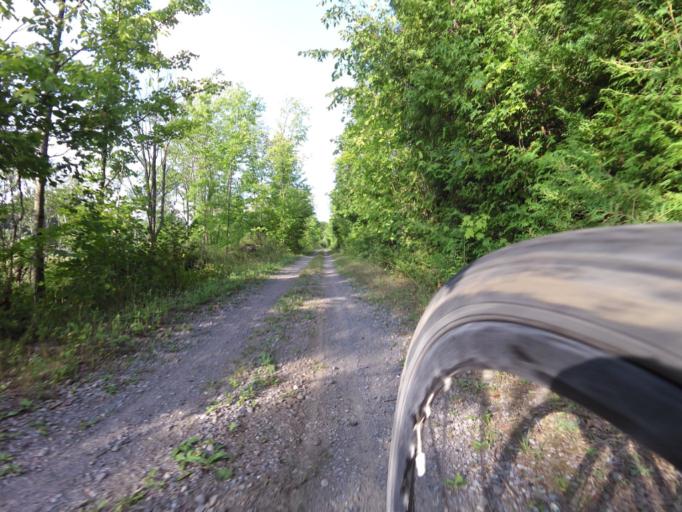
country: CA
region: Ontario
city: Kingston
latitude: 44.4765
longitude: -76.4870
